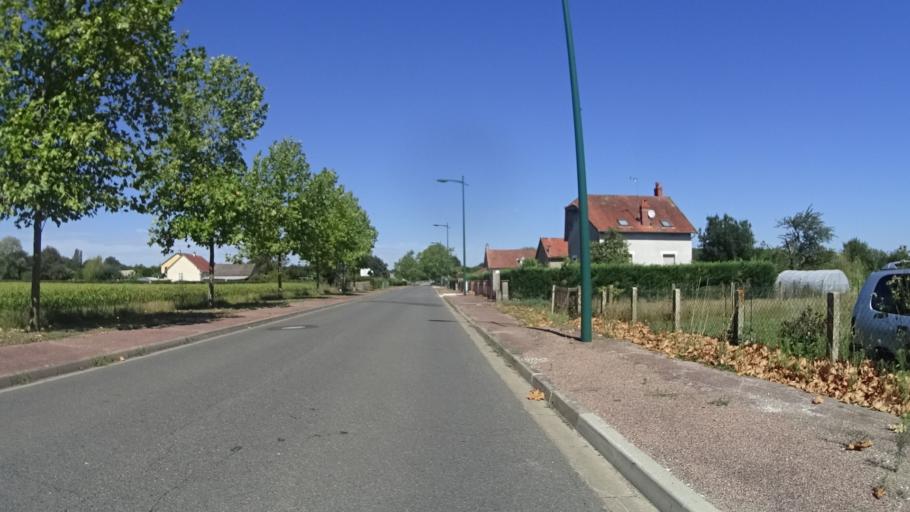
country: FR
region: Centre
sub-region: Departement du Cher
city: Belleville-sur-Loire
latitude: 47.5111
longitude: 2.8480
